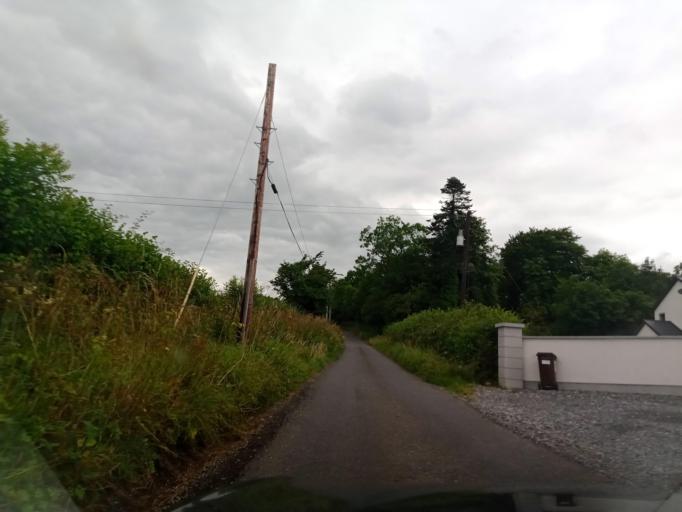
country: IE
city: Ballylinan
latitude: 52.9229
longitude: -7.0690
